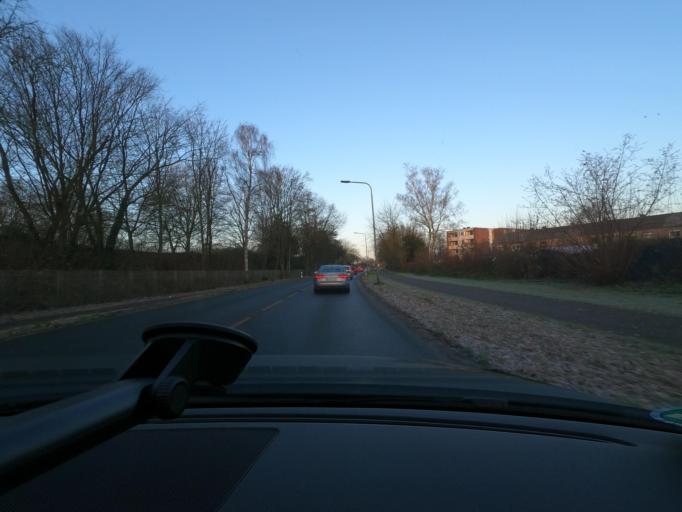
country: DE
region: North Rhine-Westphalia
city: Kempen
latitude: 51.3693
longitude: 6.4086
